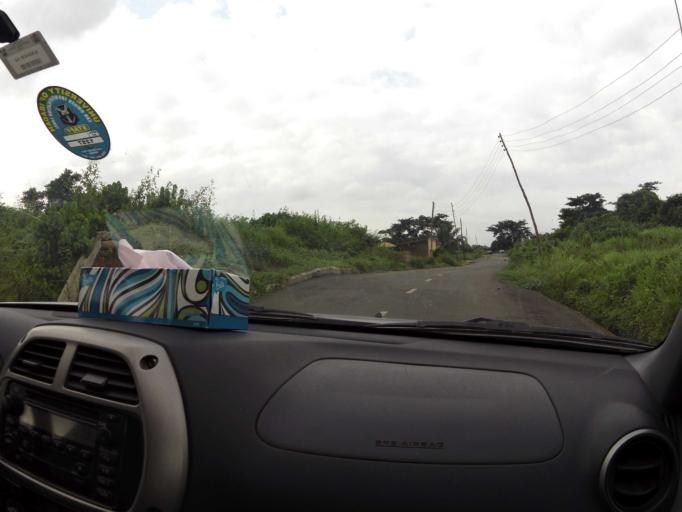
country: NG
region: Oyo
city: Moniya
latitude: 7.5275
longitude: 3.9240
